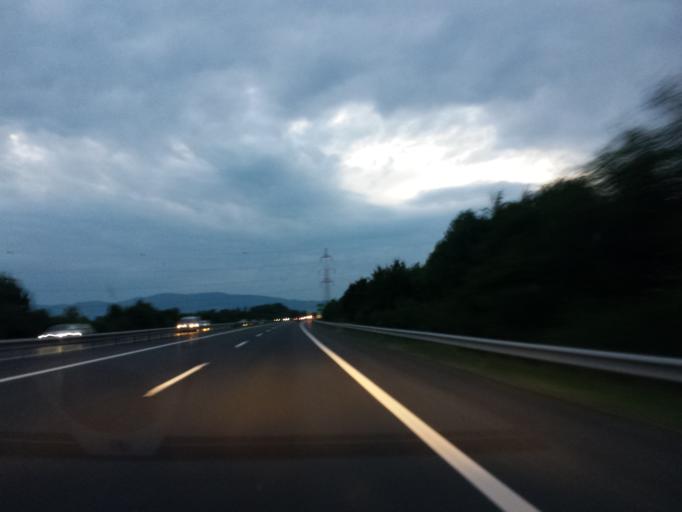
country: AT
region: Lower Austria
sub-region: Politischer Bezirk Modling
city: Munchendorf
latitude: 48.0094
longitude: 16.3740
